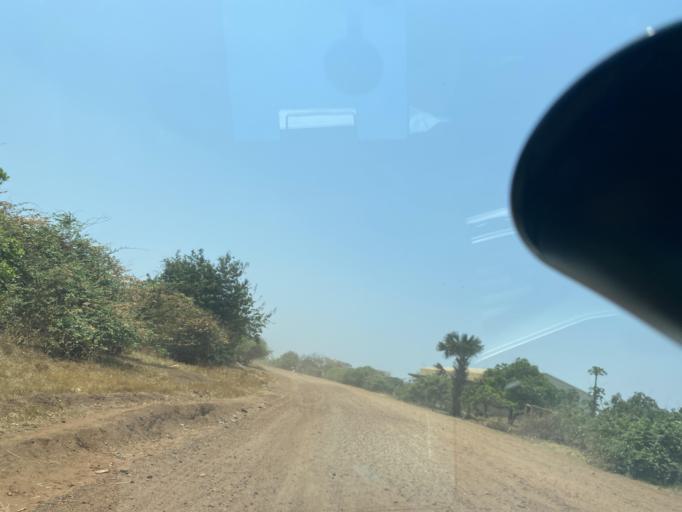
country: ZM
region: Southern
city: Nakambala
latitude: -15.4725
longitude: 27.8996
